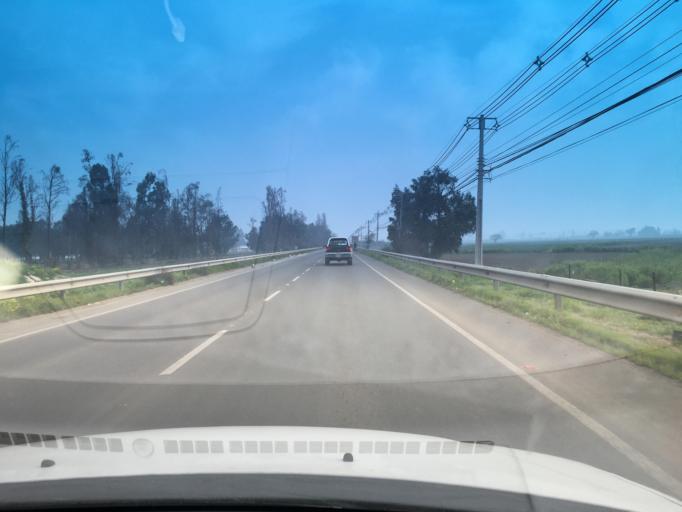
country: CL
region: Santiago Metropolitan
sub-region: Provincia de Chacabuco
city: Lampa
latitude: -33.3418
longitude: -70.8121
